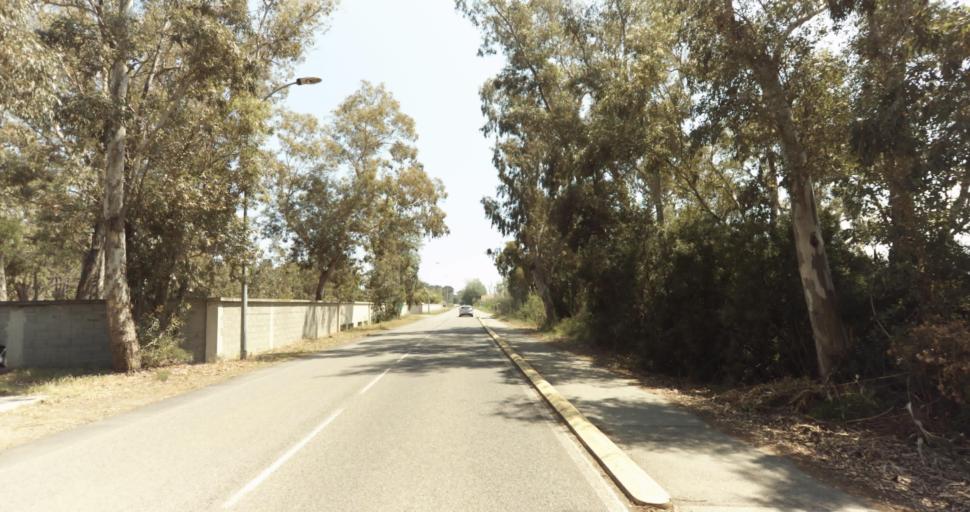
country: FR
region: Corsica
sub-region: Departement de la Haute-Corse
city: Biguglia
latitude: 42.6118
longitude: 9.4818
